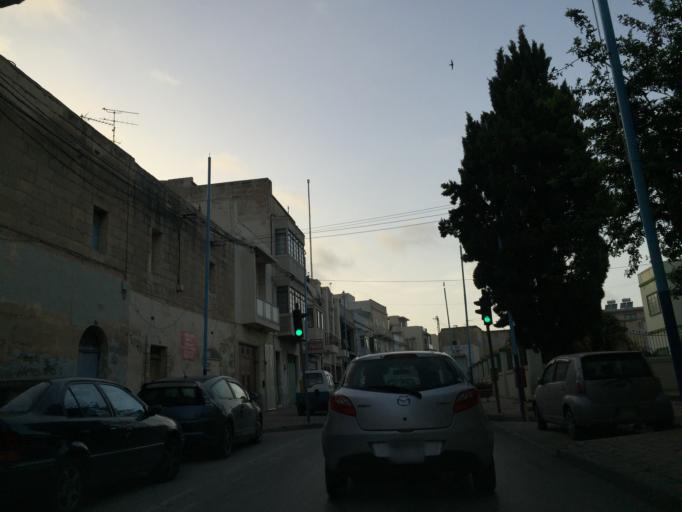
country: MT
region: Saint Paul's Bay
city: San Pawl il-Bahar
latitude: 35.9346
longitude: 14.4145
